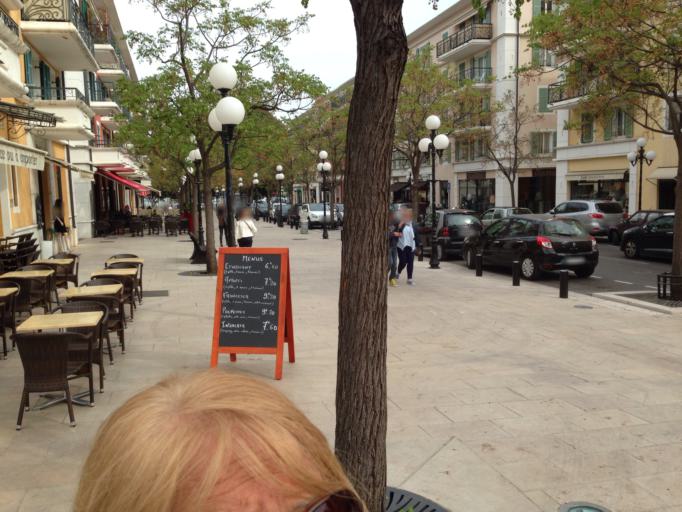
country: FR
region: Provence-Alpes-Cote d'Azur
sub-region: Departement des Alpes-Maritimes
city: Cagnes-sur-Mer
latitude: 43.6619
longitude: 7.1492
